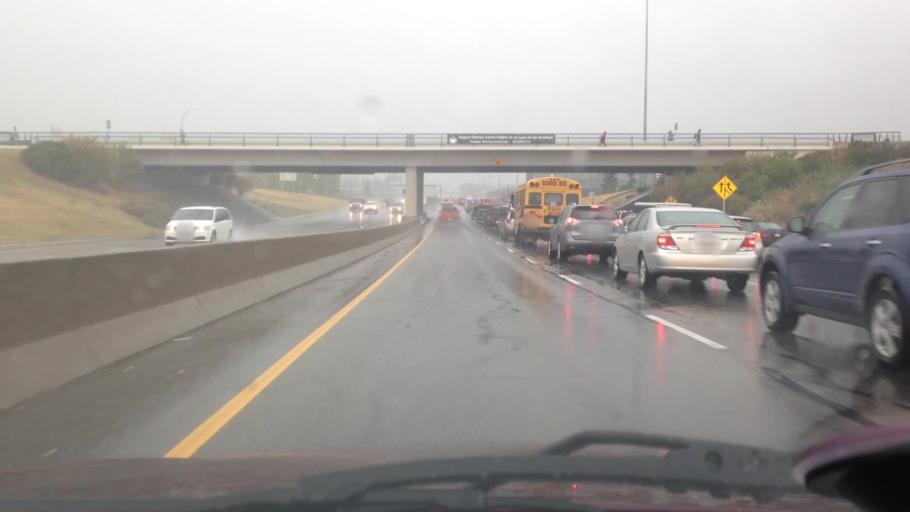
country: CA
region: Alberta
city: Calgary
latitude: 51.0097
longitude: -114.1180
